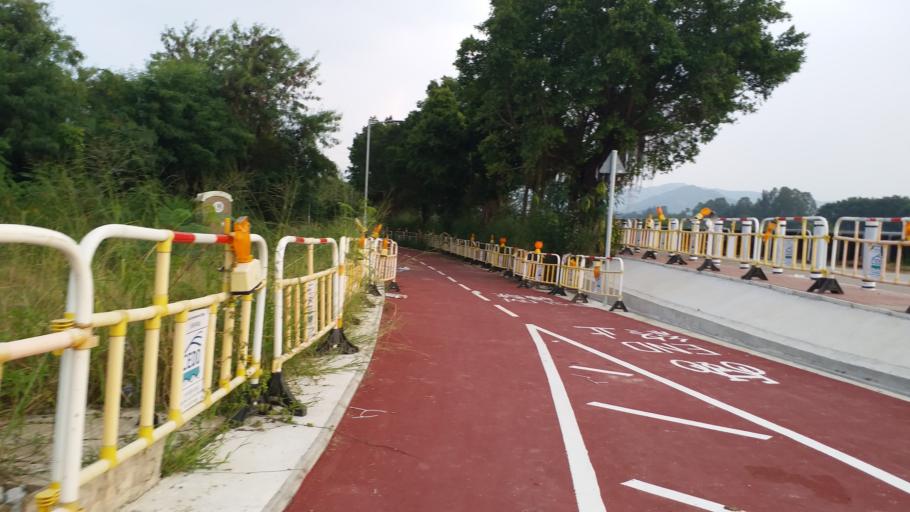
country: HK
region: Yuen Long
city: Yuen Long Kau Hui
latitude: 22.4639
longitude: 114.0449
